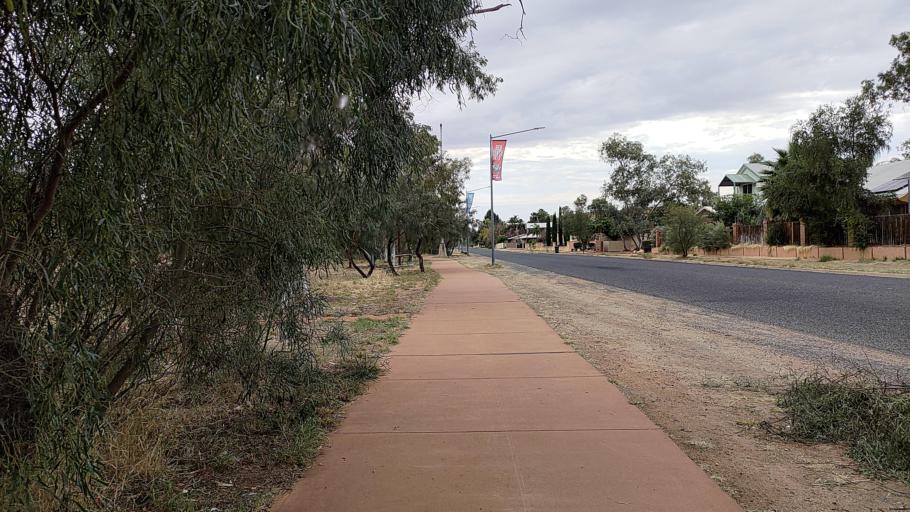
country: AU
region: Northern Territory
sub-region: Alice Springs
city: Alice Springs
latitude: -23.7122
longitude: 133.8799
